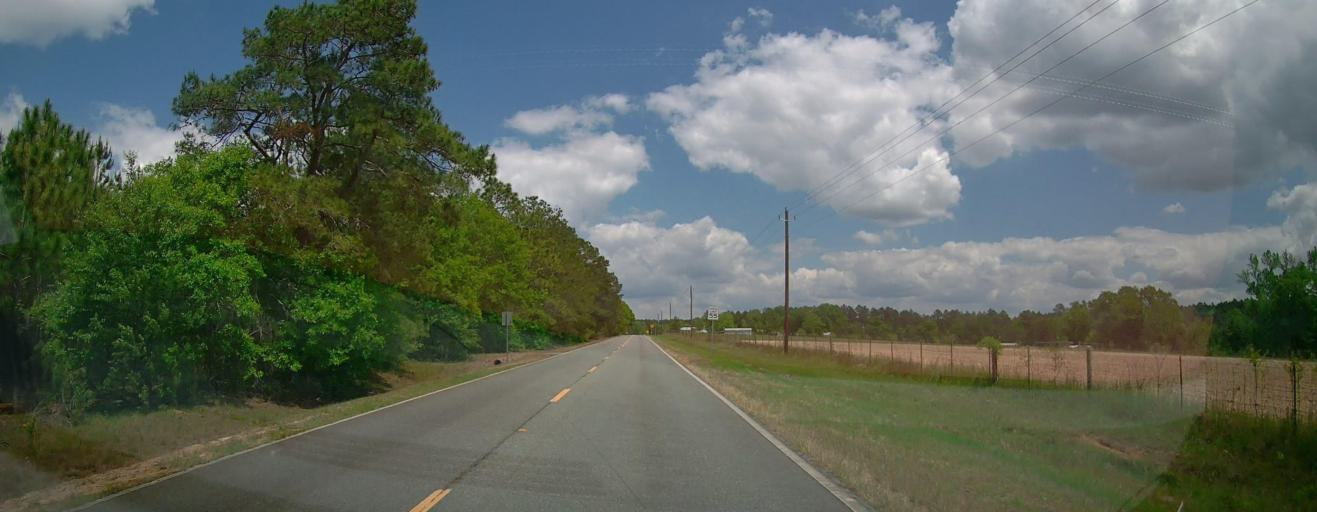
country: US
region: Georgia
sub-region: Laurens County
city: East Dublin
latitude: 32.5265
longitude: -82.7152
